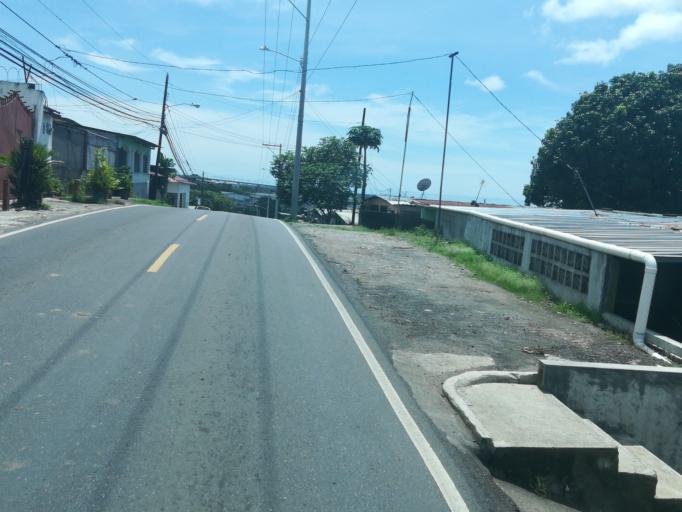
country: PA
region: Panama
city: Tocumen
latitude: 9.0935
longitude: -79.4037
